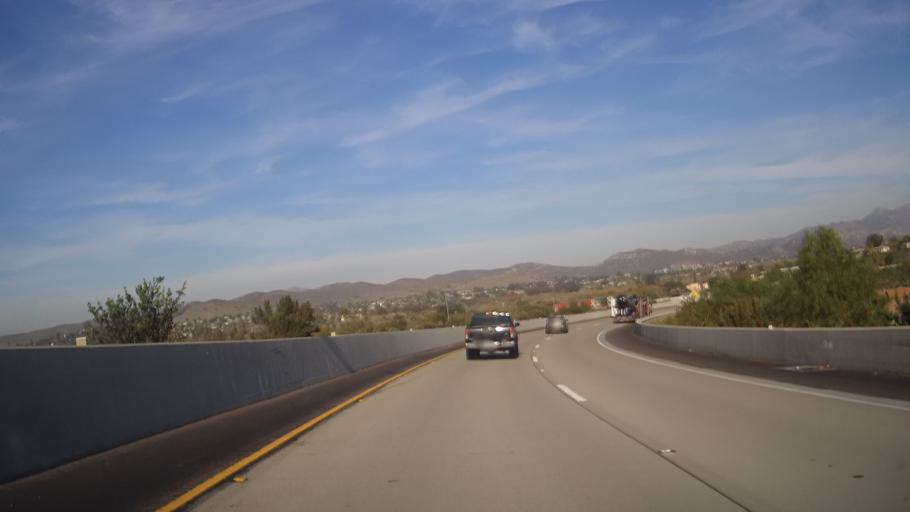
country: US
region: California
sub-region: San Diego County
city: Santee
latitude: 32.8349
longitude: -117.0021
